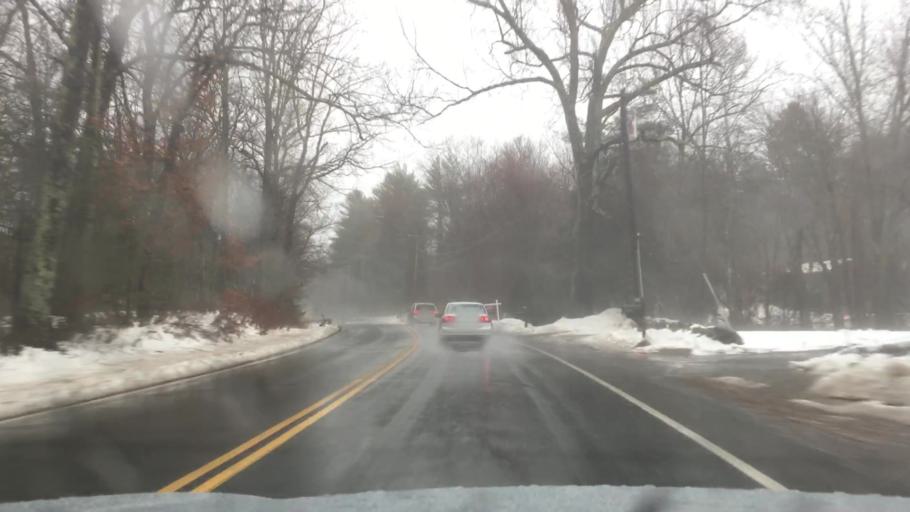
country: US
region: Massachusetts
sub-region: Hampshire County
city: Granby
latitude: 42.2410
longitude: -72.4807
